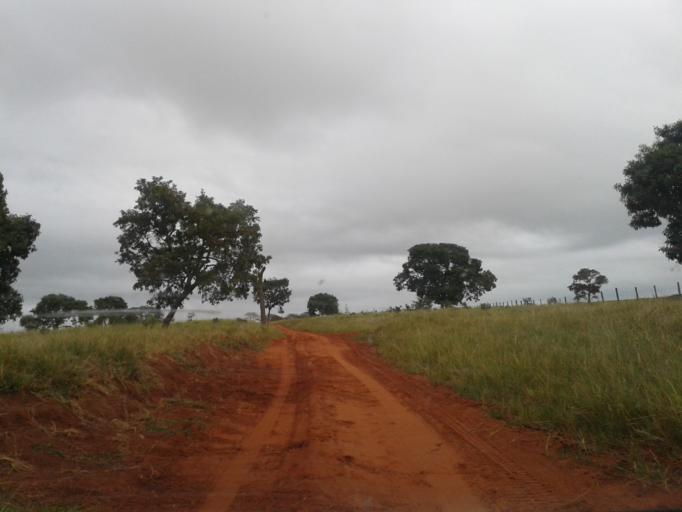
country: BR
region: Minas Gerais
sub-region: Campina Verde
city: Campina Verde
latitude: -19.4093
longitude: -49.6469
